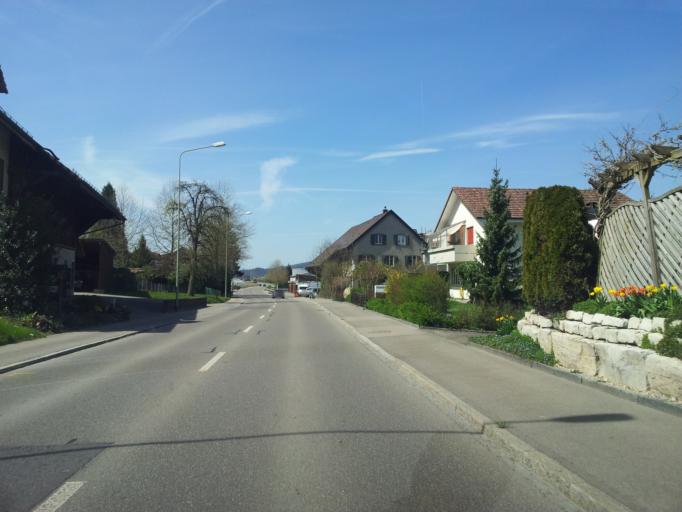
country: CH
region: Zurich
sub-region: Bezirk Dielsdorf
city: Daellikon / Daellikon (Dorf)
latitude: 47.4404
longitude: 8.4352
